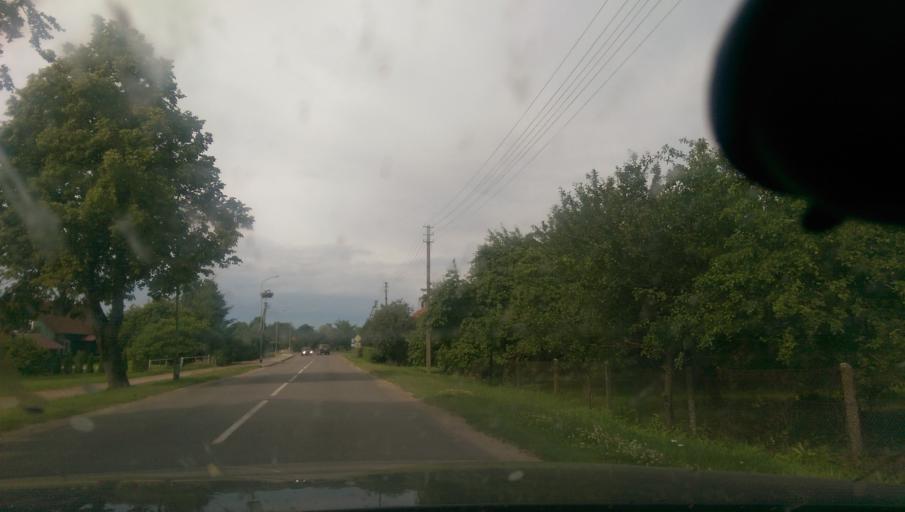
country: LT
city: Rusne
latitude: 55.3006
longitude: 21.3749
